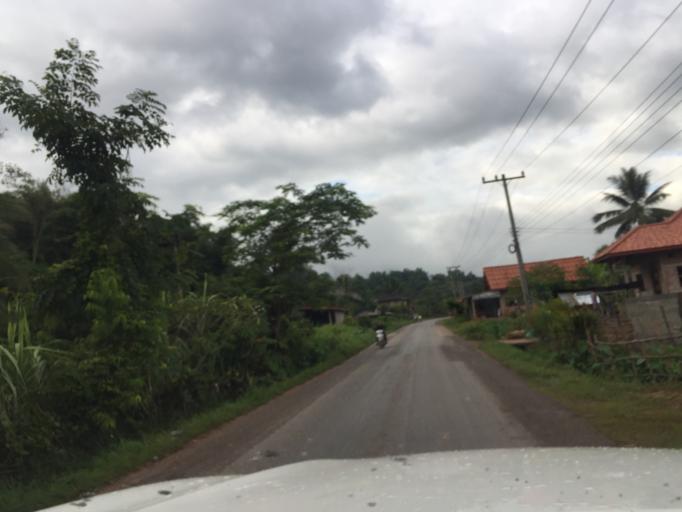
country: LA
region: Oudomxai
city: Muang La
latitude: 20.8555
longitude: 102.1102
